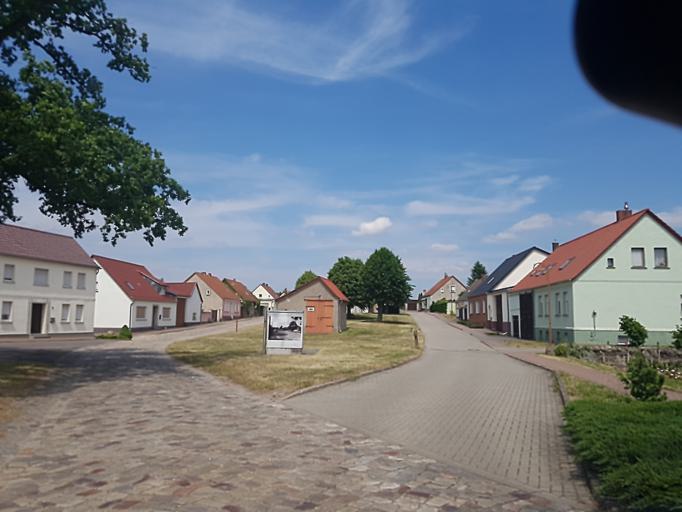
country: DE
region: Brandenburg
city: Gorzke
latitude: 52.0722
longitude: 12.3078
